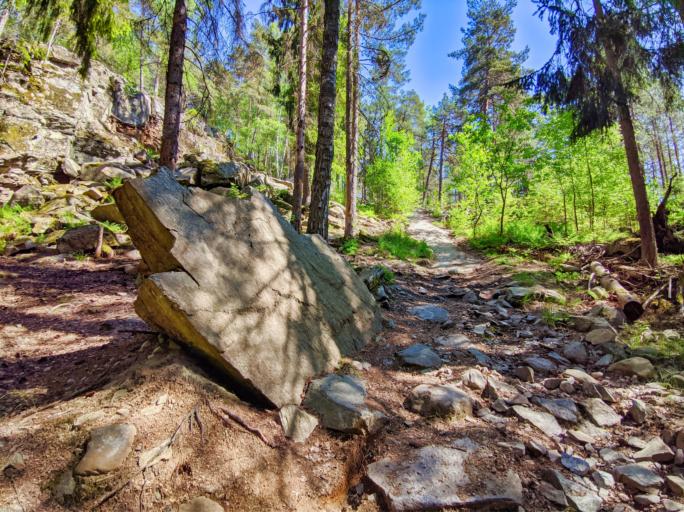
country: NO
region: Akershus
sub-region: Oppegard
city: Kolbotn
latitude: 59.8267
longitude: 10.7719
